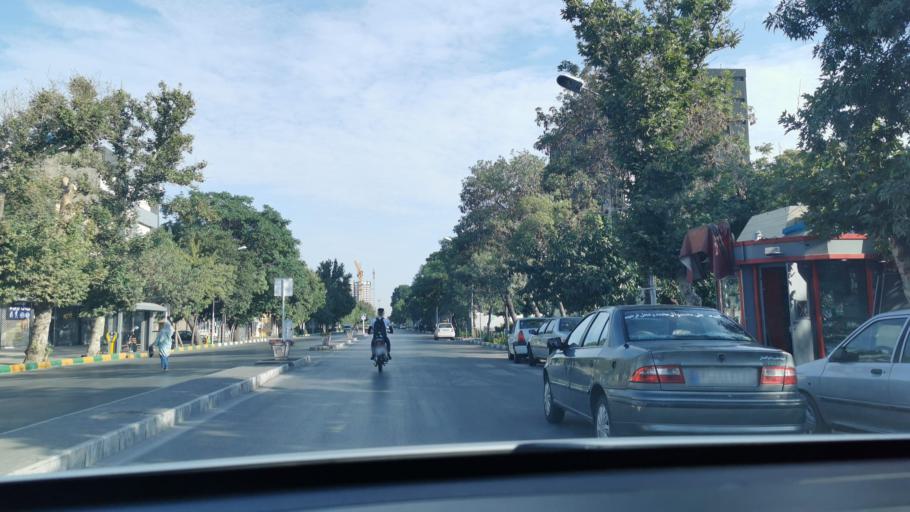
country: IR
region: Razavi Khorasan
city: Mashhad
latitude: 36.2691
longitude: 59.6079
